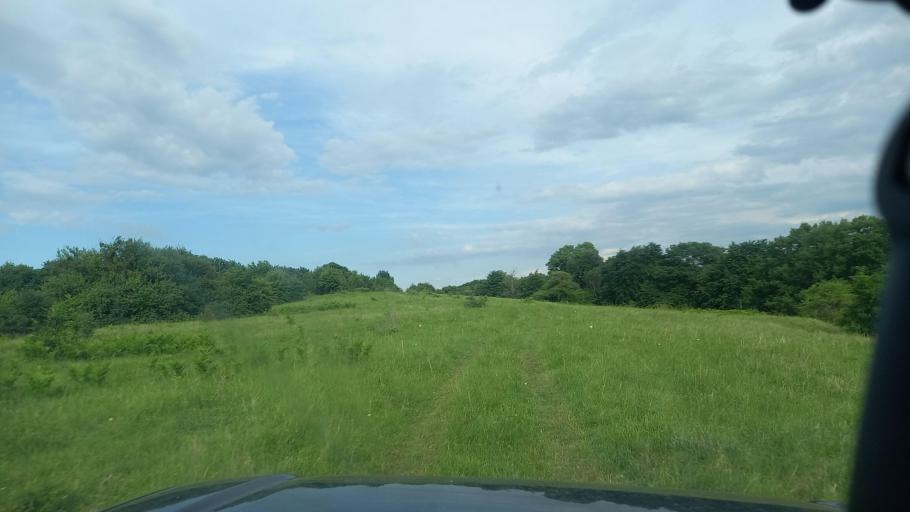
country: RU
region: Karachayevo-Cherkesiya
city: Kurdzhinovo
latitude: 44.1269
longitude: 41.0677
